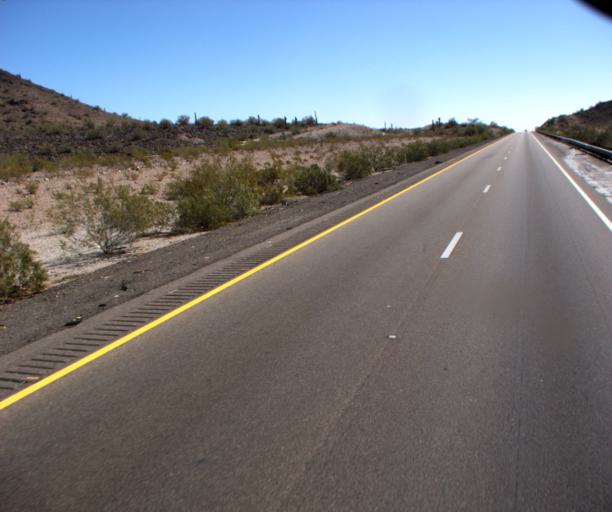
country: US
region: Arizona
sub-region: La Paz County
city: Salome
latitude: 33.6108
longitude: -113.6335
